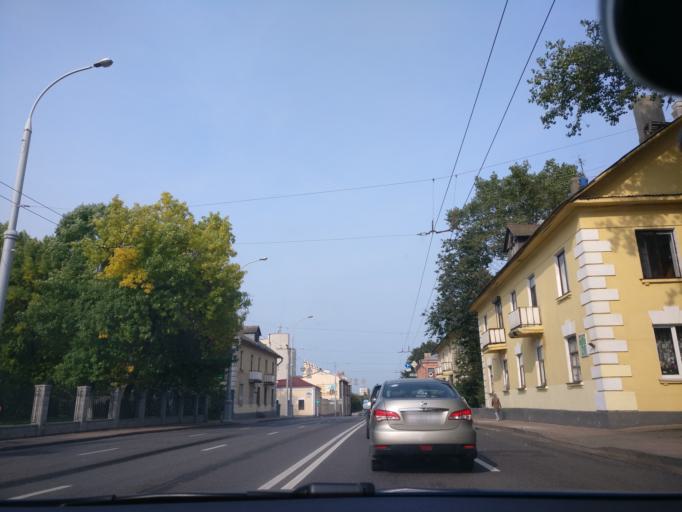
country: BY
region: Minsk
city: Minsk
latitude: 53.9141
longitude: 27.5619
